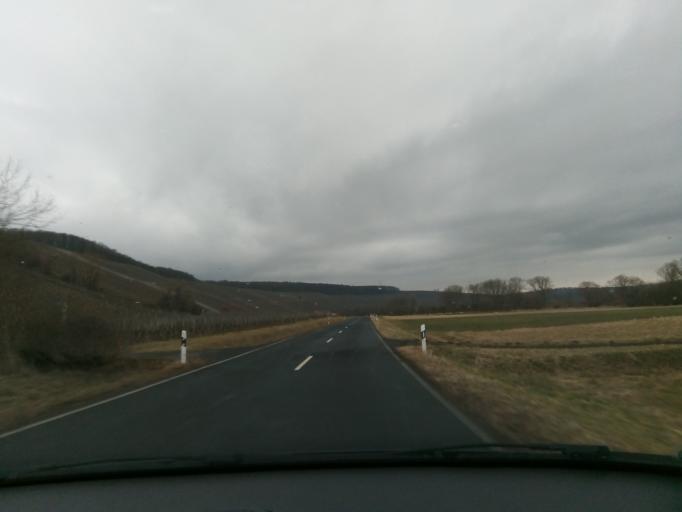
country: DE
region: Bavaria
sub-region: Regierungsbezirk Unterfranken
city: Nordheim
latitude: 49.8385
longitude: 10.1744
